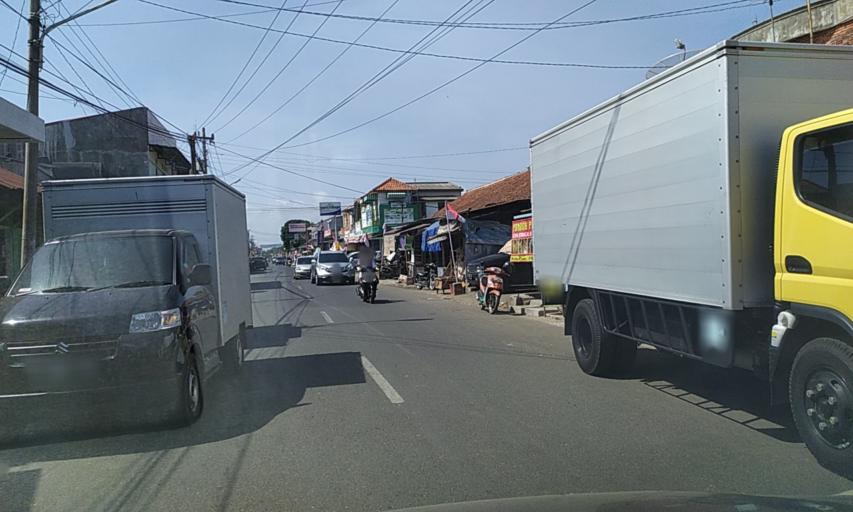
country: ID
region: Central Java
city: Karangbadar Kidul
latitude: -7.7200
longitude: 109.0114
